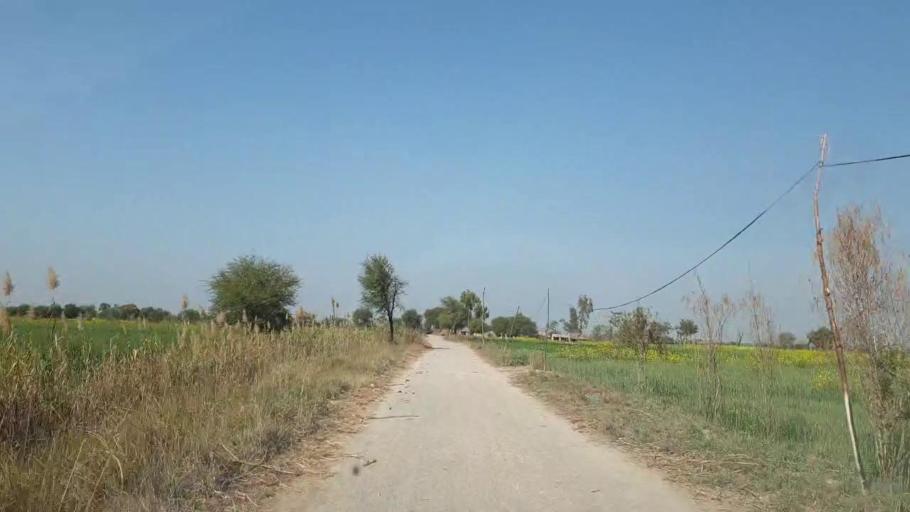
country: PK
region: Sindh
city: Mirpur Khas
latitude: 25.7280
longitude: 69.1394
